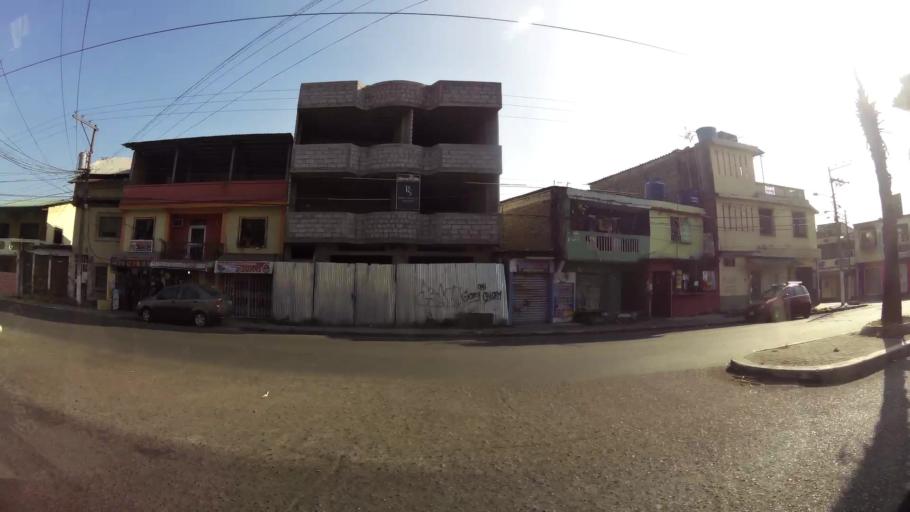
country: EC
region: Guayas
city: Eloy Alfaro
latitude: -2.1702
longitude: -79.8459
